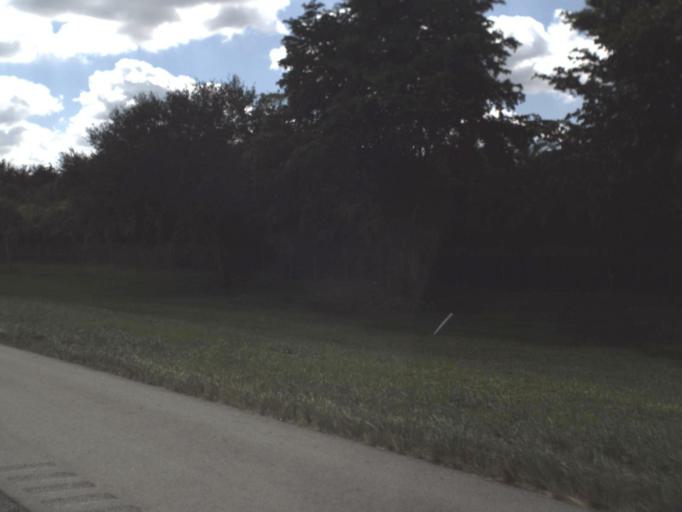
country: US
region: Florida
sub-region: Palm Beach County
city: Boca Pointe
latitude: 26.3234
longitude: -80.1703
